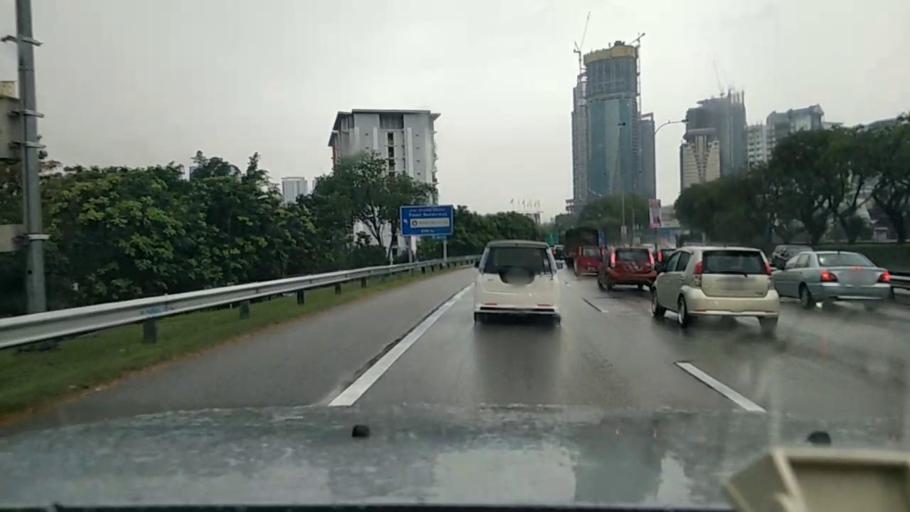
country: MY
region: Kuala Lumpur
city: Kuala Lumpur
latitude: 3.1125
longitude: 101.6826
